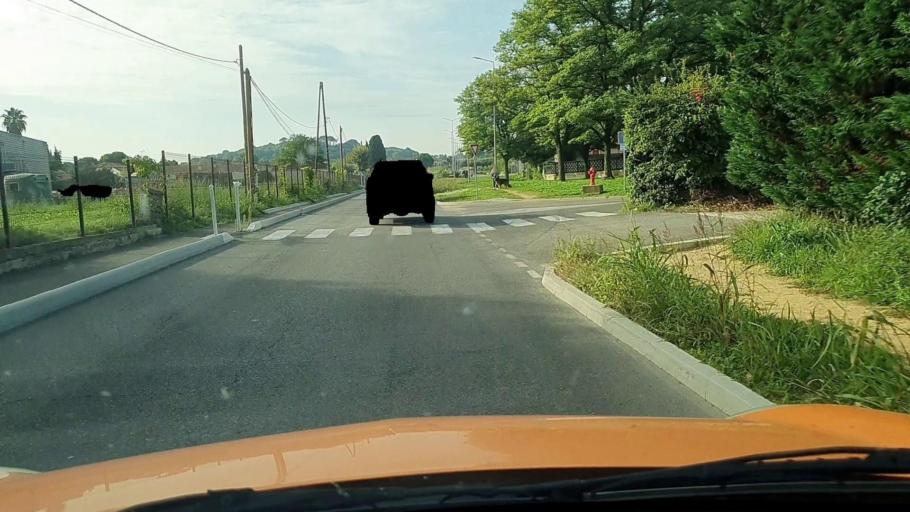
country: FR
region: Languedoc-Roussillon
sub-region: Departement du Gard
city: Generac
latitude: 43.7288
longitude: 4.3431
